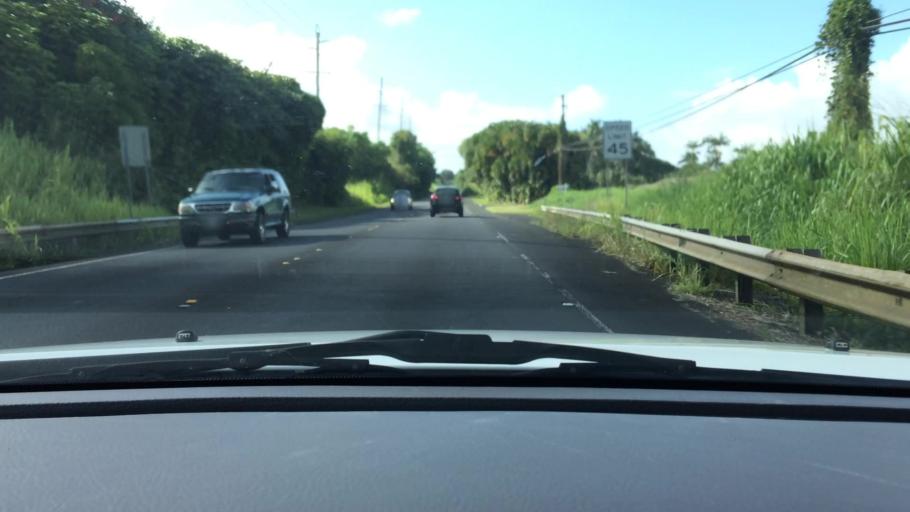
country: US
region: Hawaii
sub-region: Hawaii County
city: Papa'ikou
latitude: 19.7677
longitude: -155.0917
